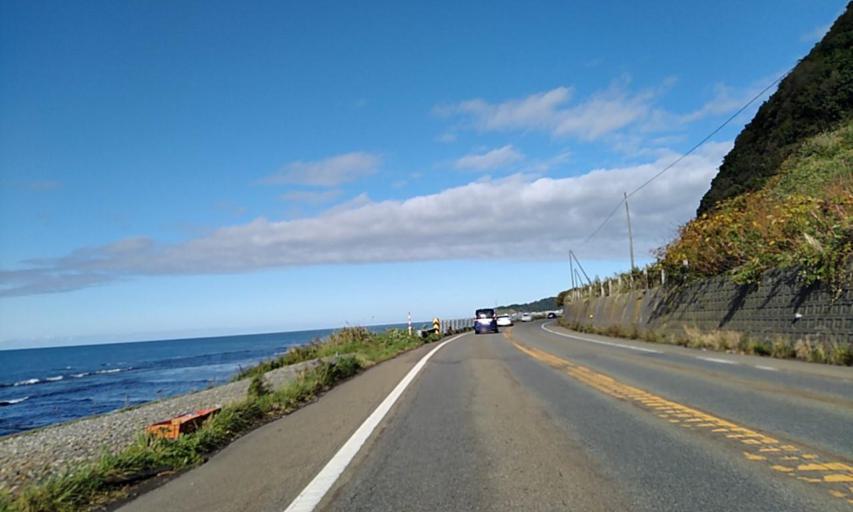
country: JP
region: Hokkaido
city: Shizunai-furukawacho
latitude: 42.2597
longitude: 142.5242
